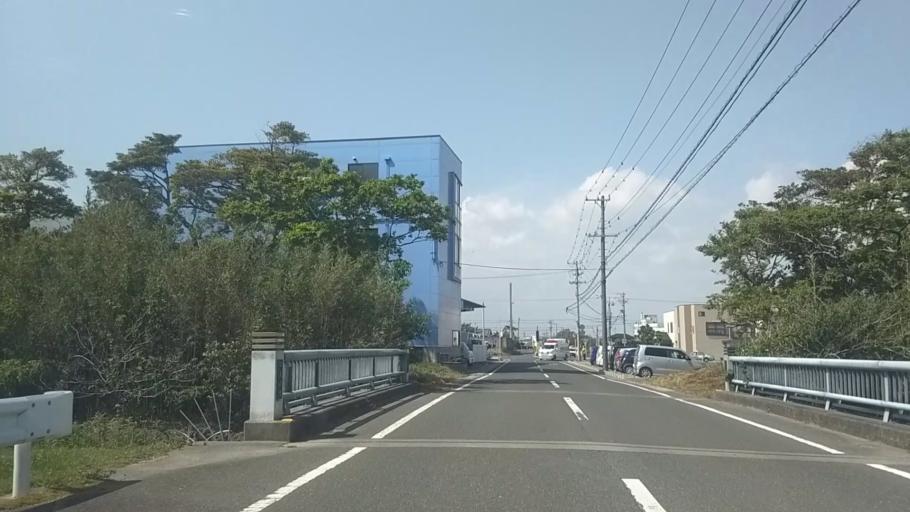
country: JP
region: Shizuoka
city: Hamamatsu
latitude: 34.6684
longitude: 137.7225
